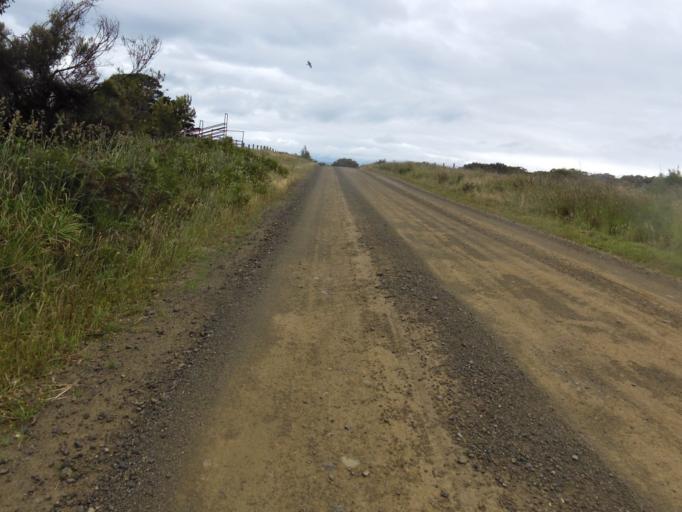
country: AU
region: Victoria
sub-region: Bass Coast
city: Cowes
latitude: -38.3820
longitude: 145.3683
